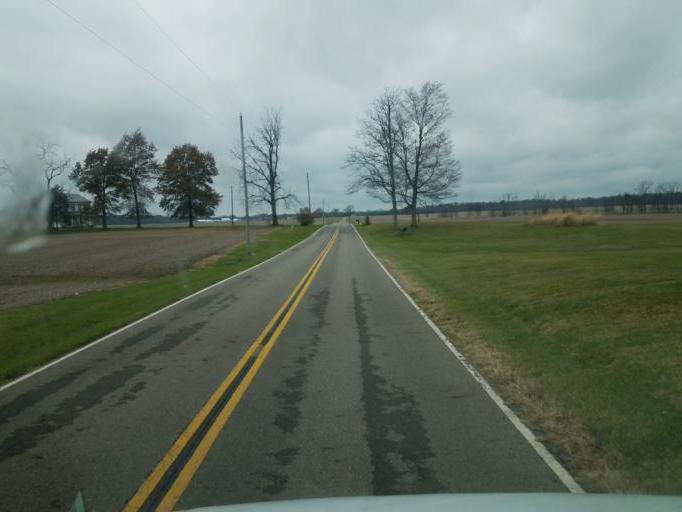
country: US
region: Ohio
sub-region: Licking County
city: Johnstown
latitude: 40.2216
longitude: -82.6291
